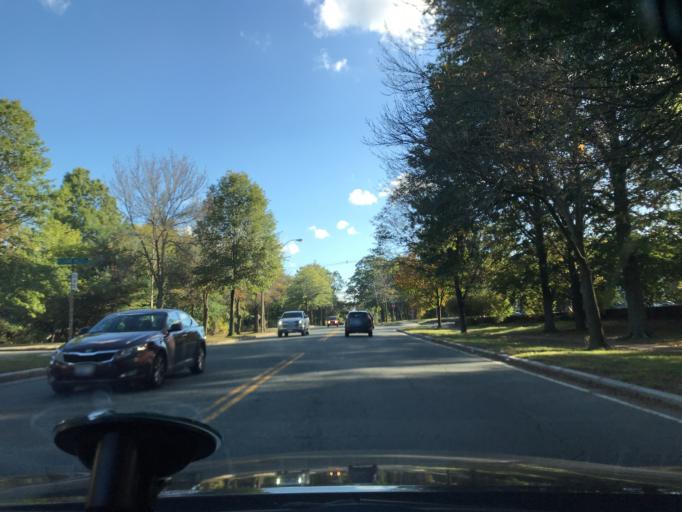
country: US
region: Massachusetts
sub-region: Suffolk County
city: Jamaica Plain
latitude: 42.2910
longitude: -71.1470
